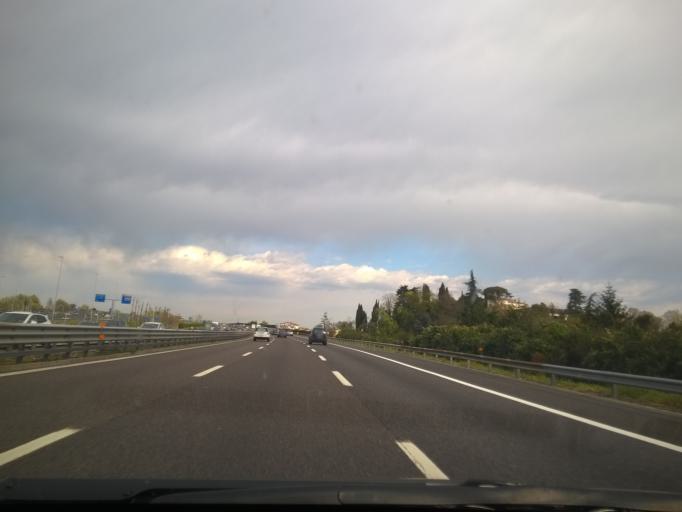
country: IT
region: Veneto
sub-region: Provincia di Vicenza
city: Arcugnano-Torri
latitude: 45.5156
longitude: 11.5586
